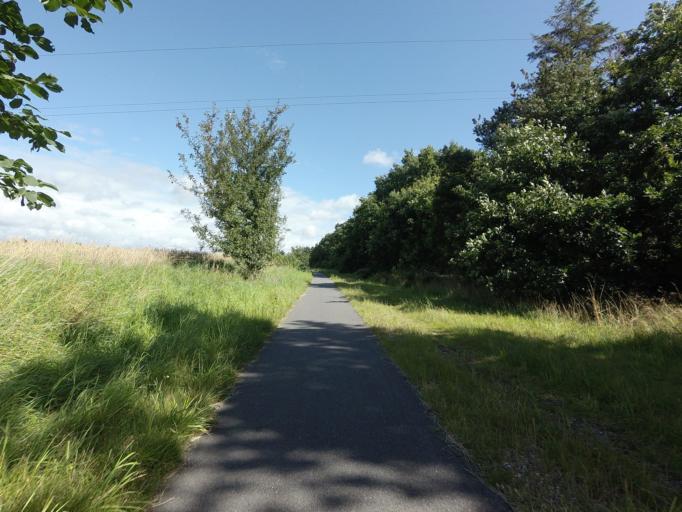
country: DK
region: Central Jutland
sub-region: Silkeborg Kommune
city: Svejbaek
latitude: 56.1883
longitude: 9.6607
